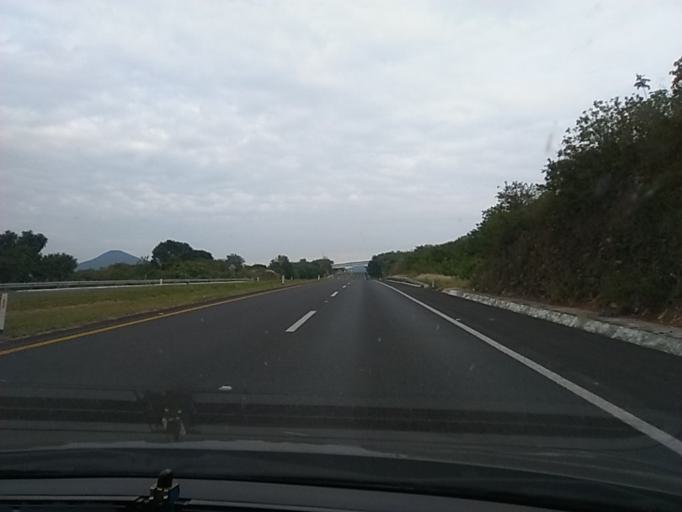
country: MX
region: Michoacan
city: Panindicuaro de la Reforma
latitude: 19.9744
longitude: -101.7413
